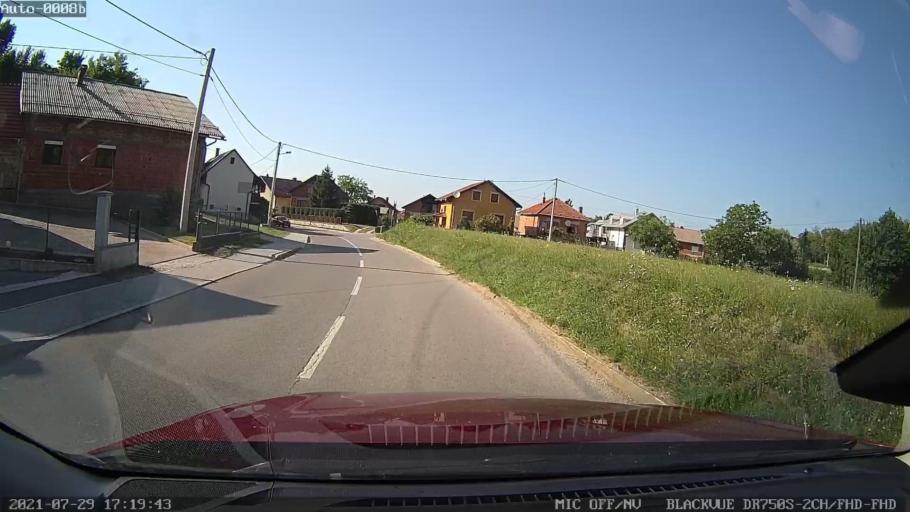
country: HR
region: Varazdinska
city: Ivanec
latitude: 46.2164
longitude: 16.1265
